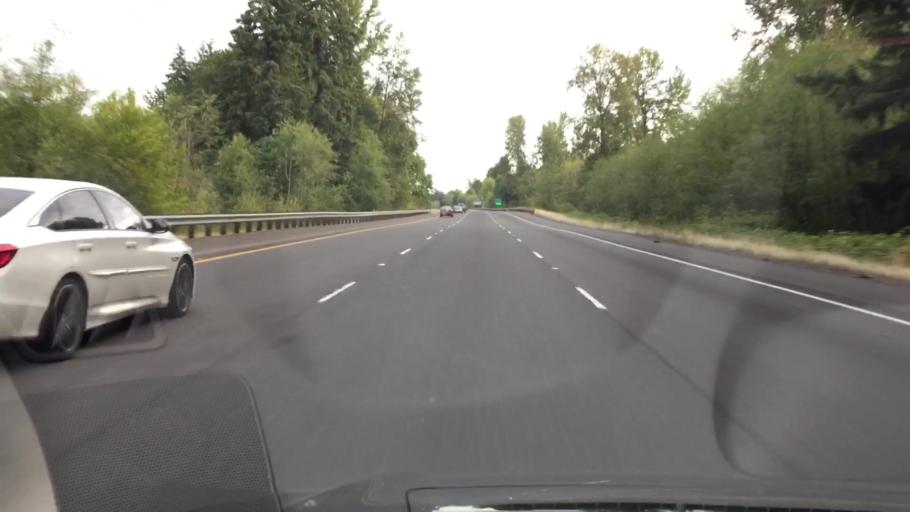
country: US
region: Washington
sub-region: Cowlitz County
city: West Side Highway
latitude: 46.2166
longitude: -122.8915
